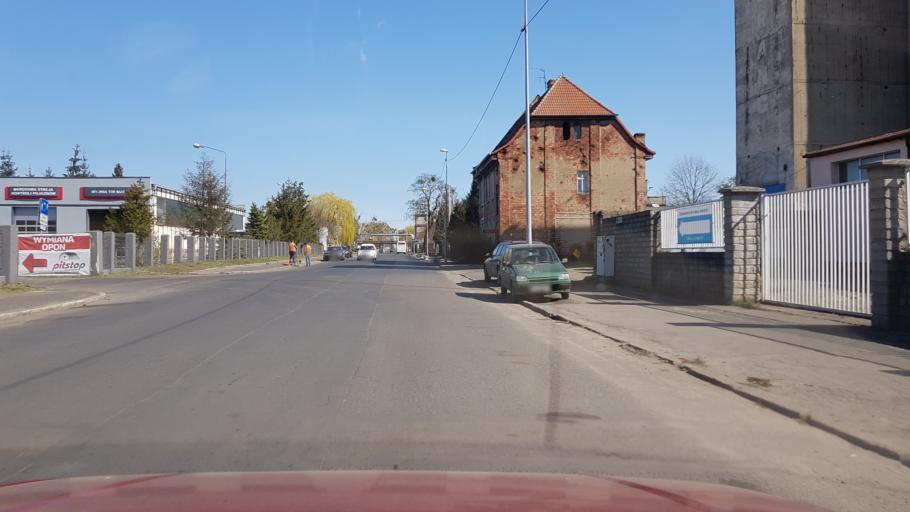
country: PL
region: West Pomeranian Voivodeship
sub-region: Szczecin
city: Szczecin
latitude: 53.4164
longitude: 14.5562
